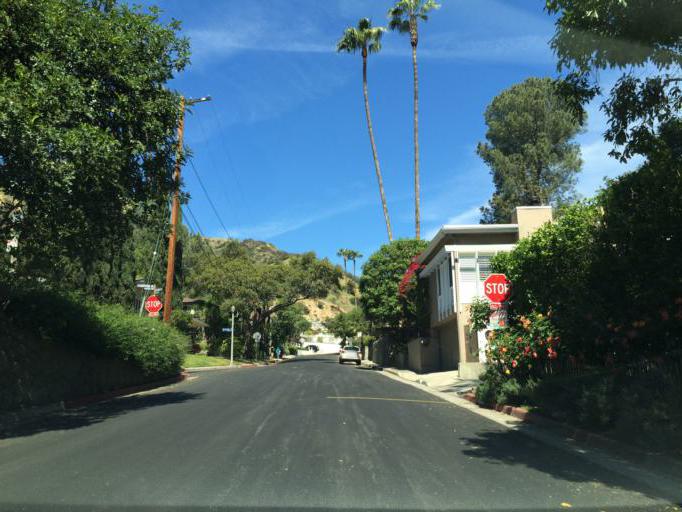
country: US
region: California
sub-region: Los Angeles County
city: Hollywood
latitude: 34.1257
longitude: -118.3178
